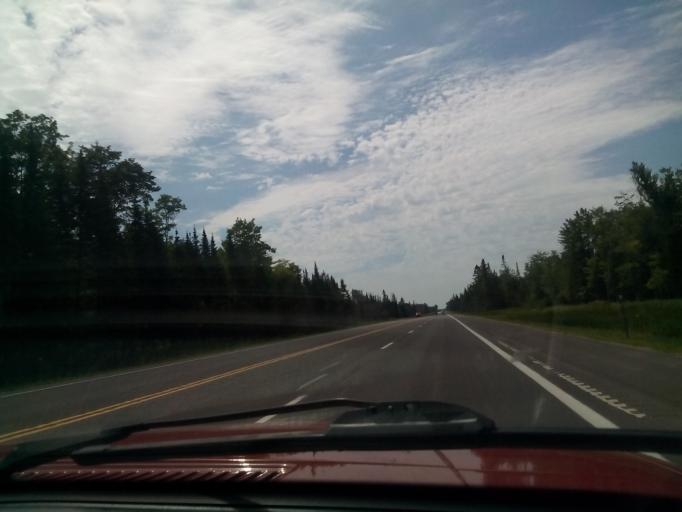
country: US
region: Michigan
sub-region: Schoolcraft County
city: Manistique
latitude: 46.0260
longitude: -85.9839
